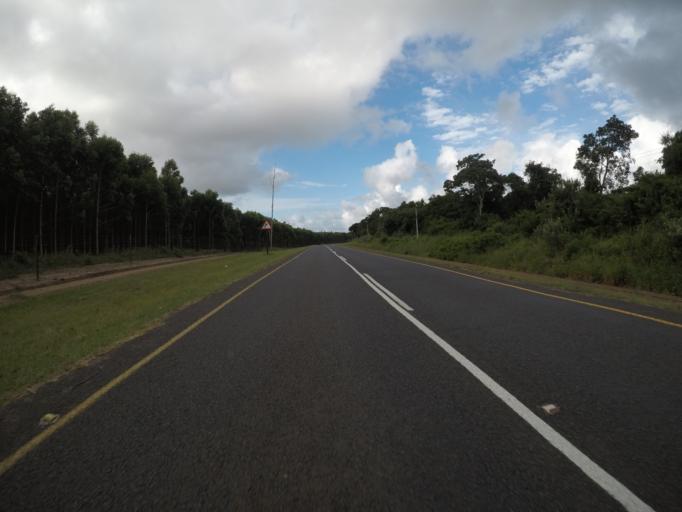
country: ZA
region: KwaZulu-Natal
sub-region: uMkhanyakude District Municipality
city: Mtubatuba
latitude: -28.3726
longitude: 32.2540
